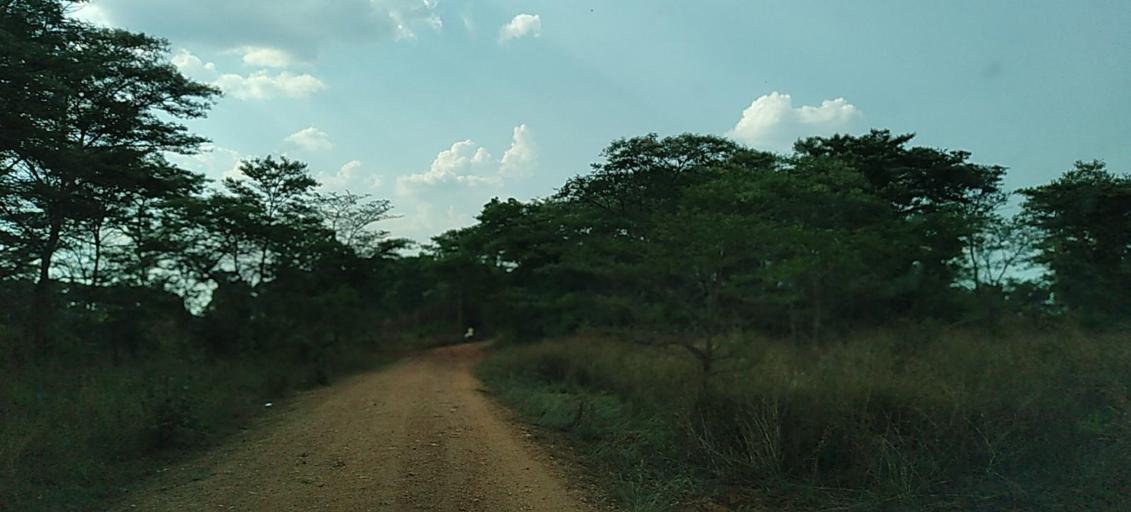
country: ZM
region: Copperbelt
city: Mpongwe
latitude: -13.5089
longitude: 28.0927
